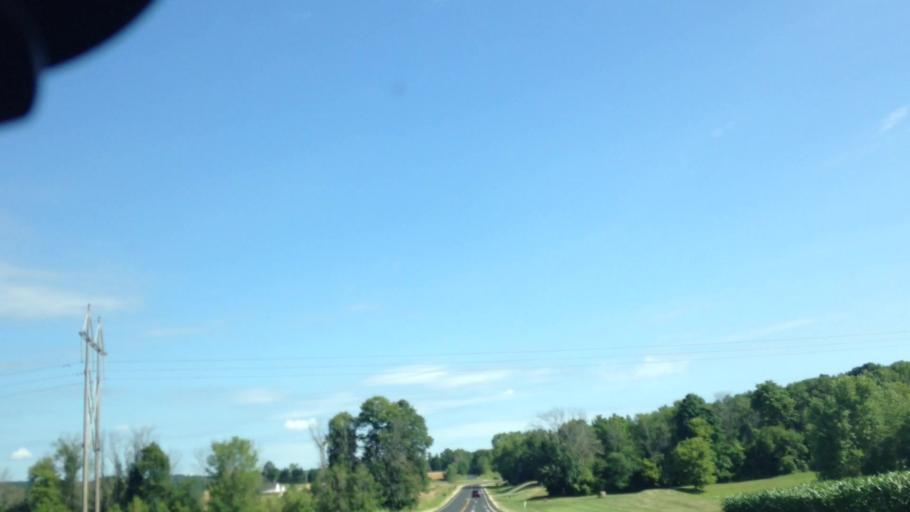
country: US
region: Wisconsin
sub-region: Washington County
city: Slinger
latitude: 43.3588
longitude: -88.2609
